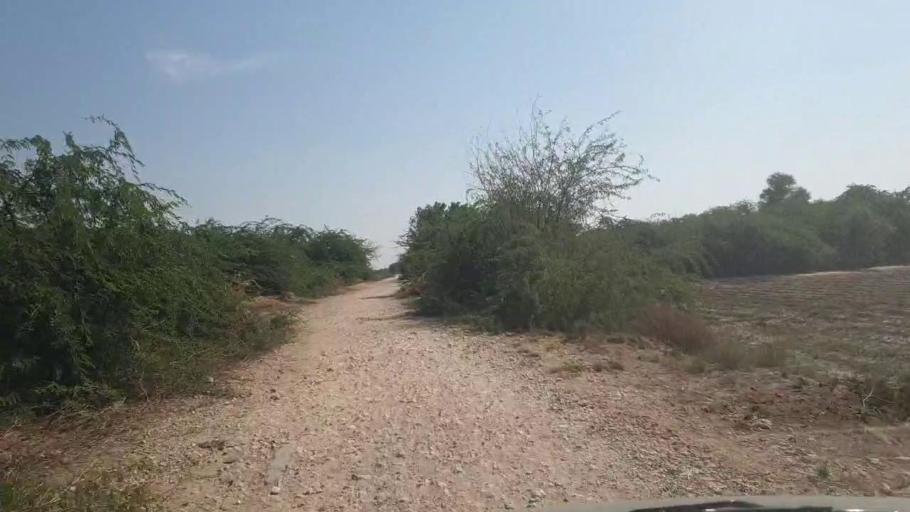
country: PK
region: Sindh
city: Digri
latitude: 24.9474
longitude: 69.1535
